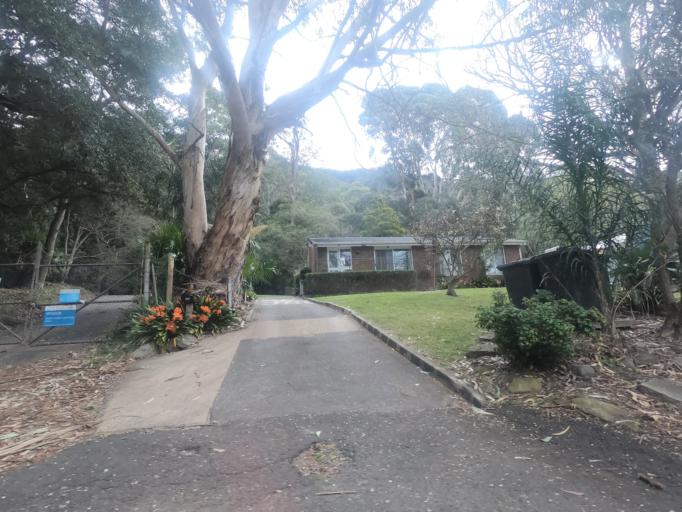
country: AU
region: New South Wales
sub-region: Wollongong
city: Bulli
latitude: -34.2927
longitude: 150.9359
